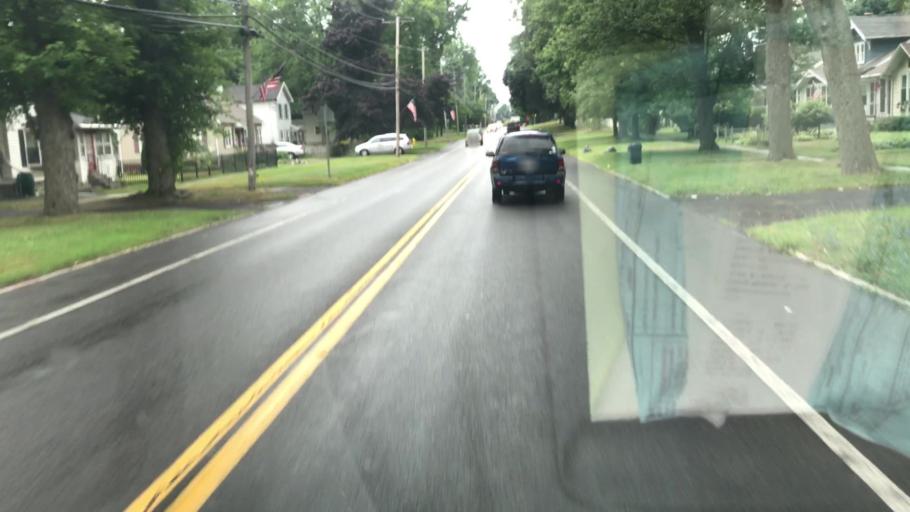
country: US
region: New York
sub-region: Onondaga County
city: Liverpool
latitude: 43.1091
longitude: -76.2104
